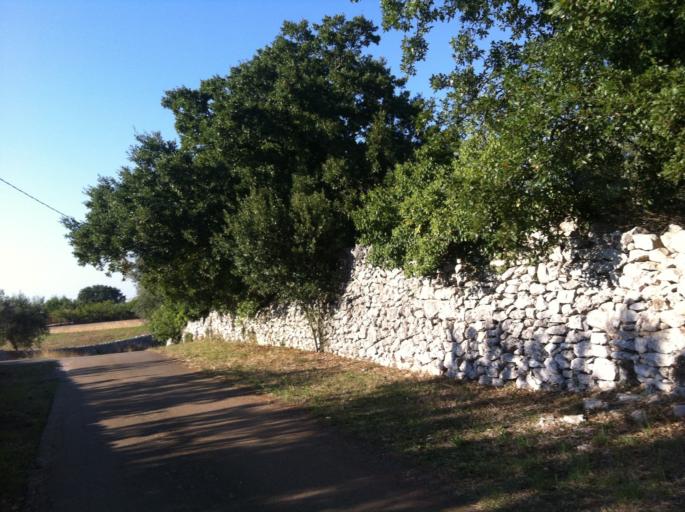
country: IT
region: Apulia
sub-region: Provincia di Bari
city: Putignano
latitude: 40.8242
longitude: 17.1392
